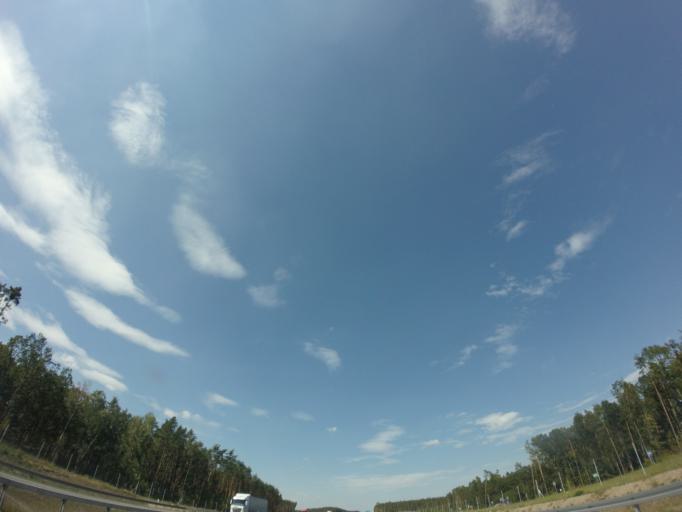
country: PL
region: Lower Silesian Voivodeship
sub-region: Powiat lubinski
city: Osiek
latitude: 51.3273
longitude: 16.1624
